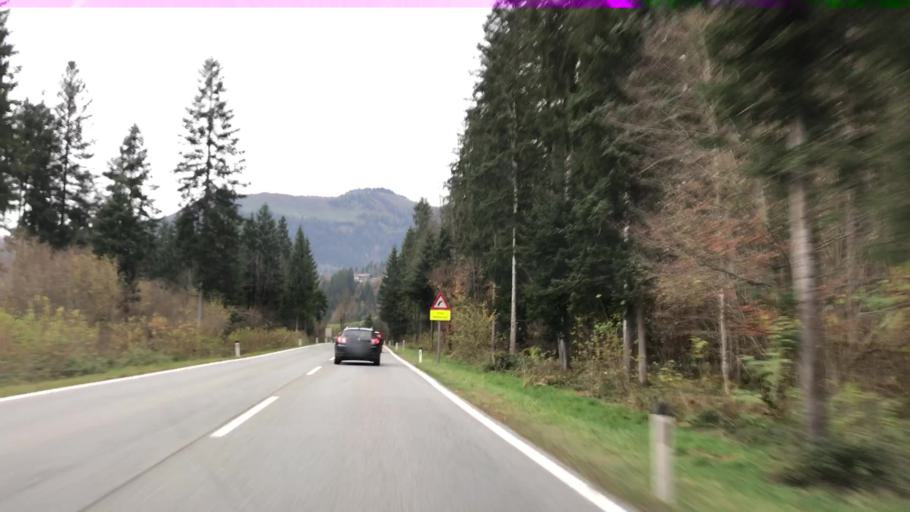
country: AT
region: Tyrol
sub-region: Politischer Bezirk Kitzbuhel
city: Kossen
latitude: 47.6590
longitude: 12.4254
